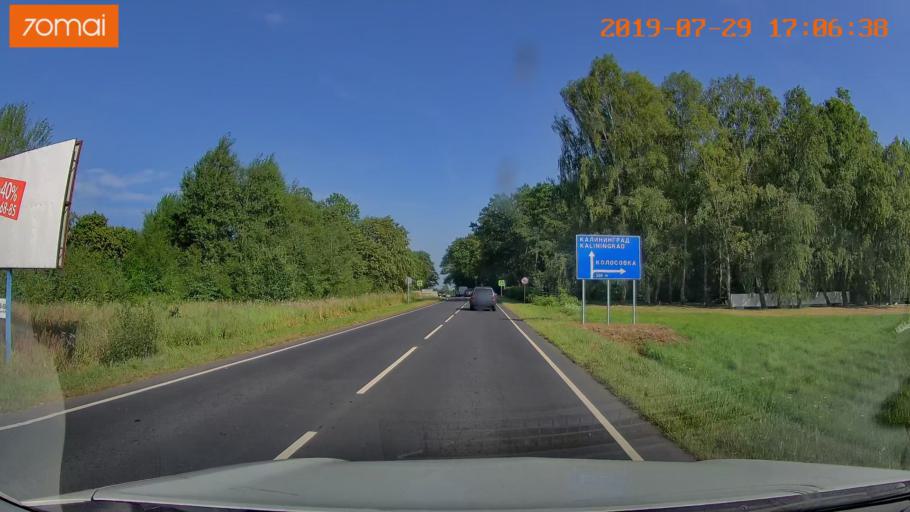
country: RU
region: Kaliningrad
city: Vzmorye
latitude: 54.8195
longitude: 20.3109
